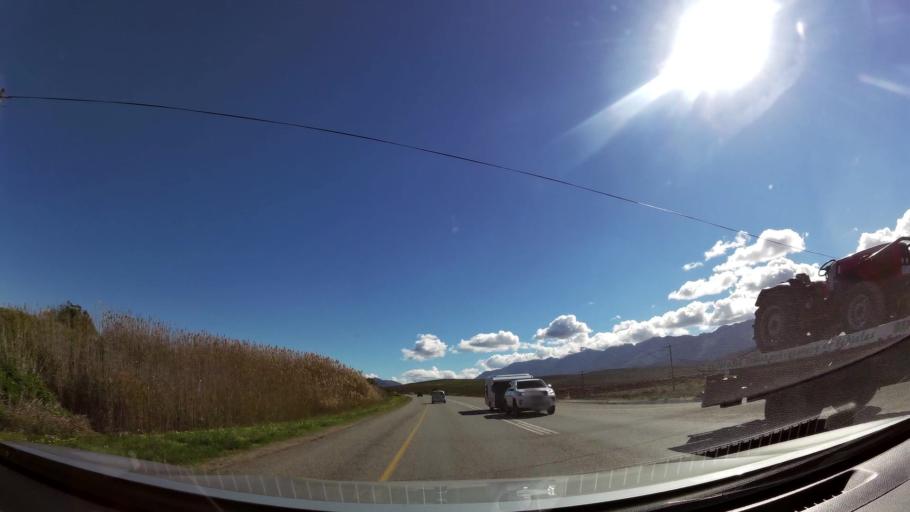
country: ZA
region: Western Cape
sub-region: Cape Winelands District Municipality
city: Ashton
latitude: -33.8207
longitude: 19.9729
